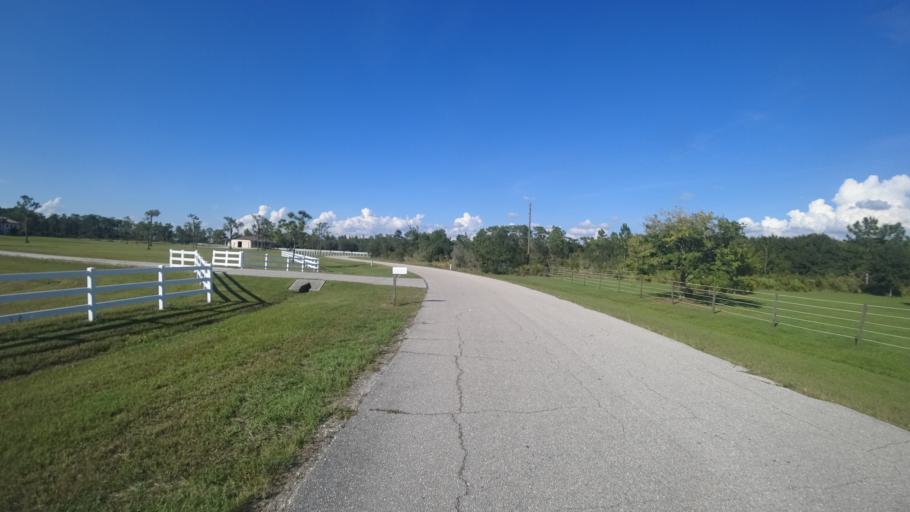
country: US
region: Florida
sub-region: Sarasota County
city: Lake Sarasota
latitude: 27.3953
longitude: -82.2835
